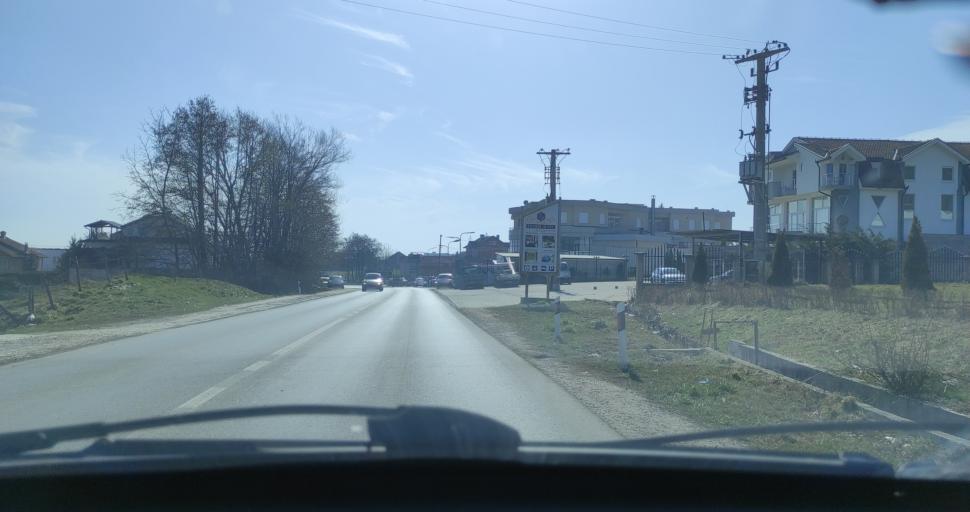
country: XK
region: Gjakova
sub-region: Komuna e Decanit
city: Lebushe
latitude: 42.5552
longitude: 20.2898
